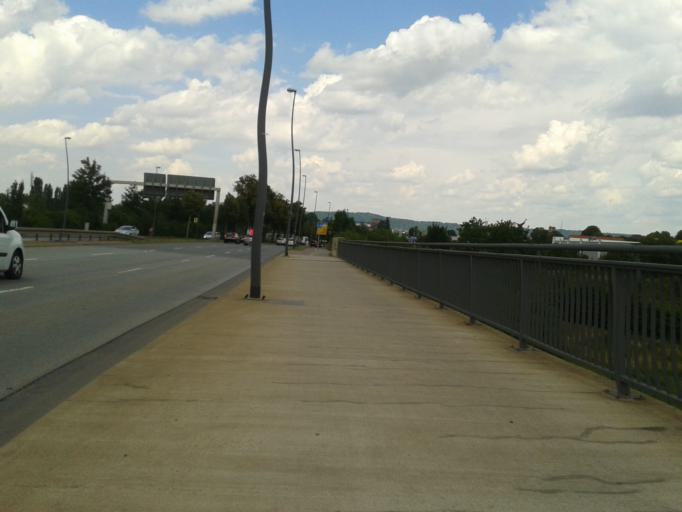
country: DE
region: Saxony
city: Radebeul
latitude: 51.0653
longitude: 13.6898
